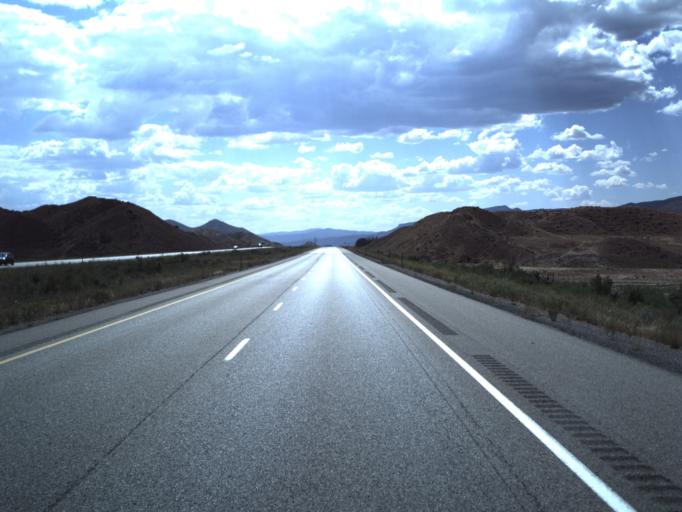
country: US
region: Utah
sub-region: Sevier County
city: Aurora
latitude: 38.9132
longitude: -111.8872
